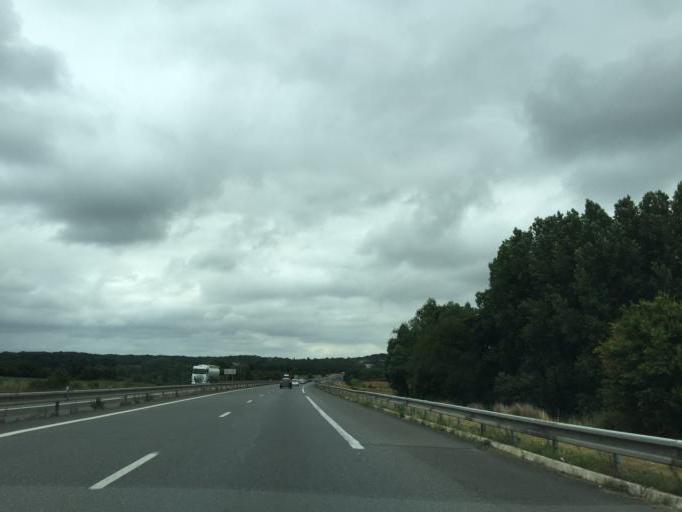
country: FR
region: Pays de la Loire
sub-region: Departement de la Mayenne
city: Saint-Pierre-la-Cour
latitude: 48.0825
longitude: -1.0133
